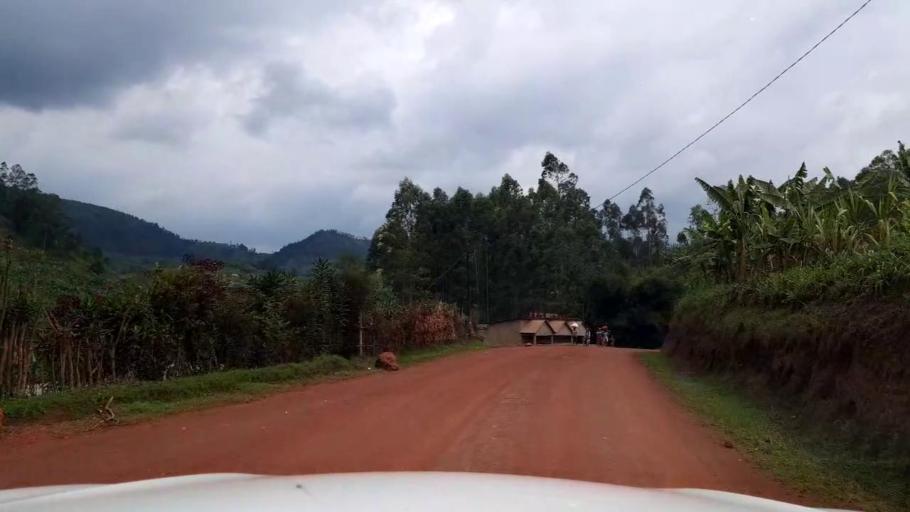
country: RW
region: Northern Province
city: Musanze
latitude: -1.6588
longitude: 29.7999
